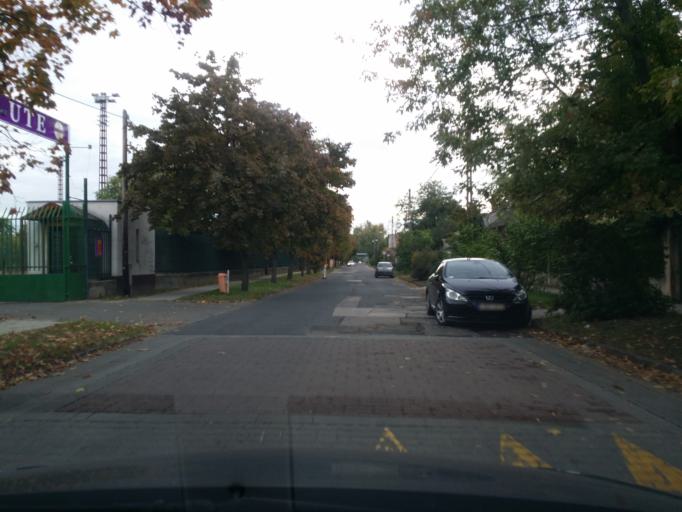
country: HU
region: Budapest
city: Budapest XV. keruelet
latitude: 47.5730
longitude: 19.1080
